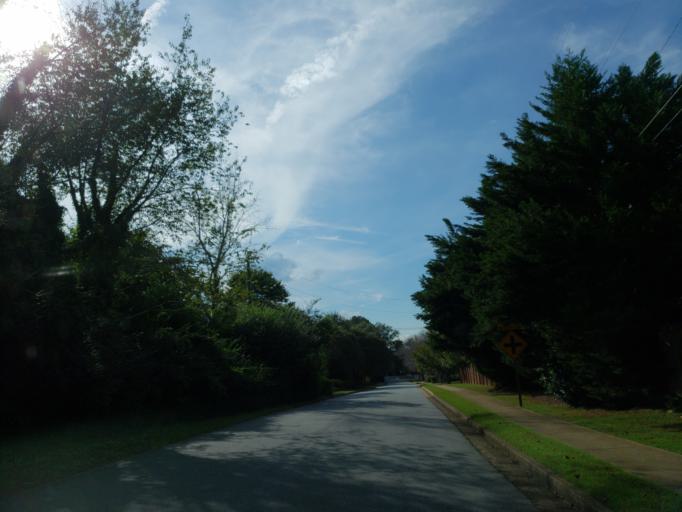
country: US
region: Georgia
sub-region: Cherokee County
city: Woodstock
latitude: 34.0490
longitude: -84.4866
